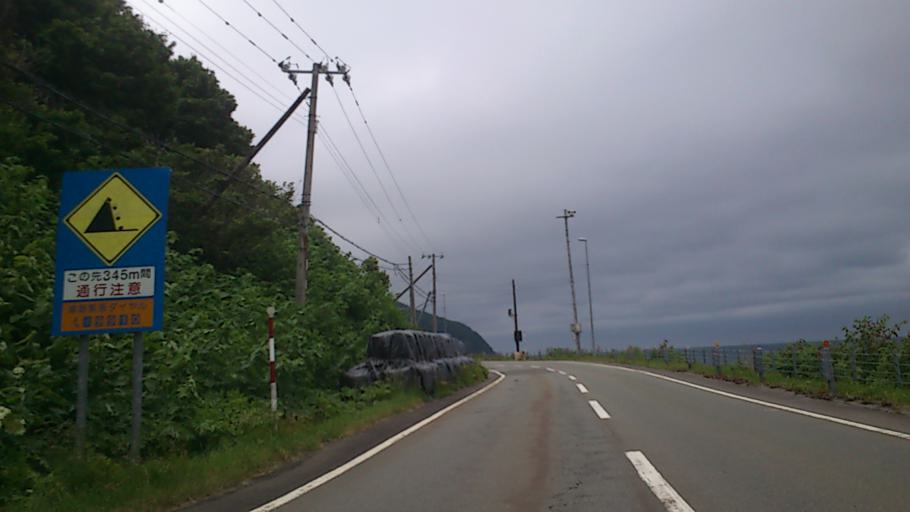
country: JP
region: Hokkaido
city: Iwanai
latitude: 42.6906
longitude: 139.9712
